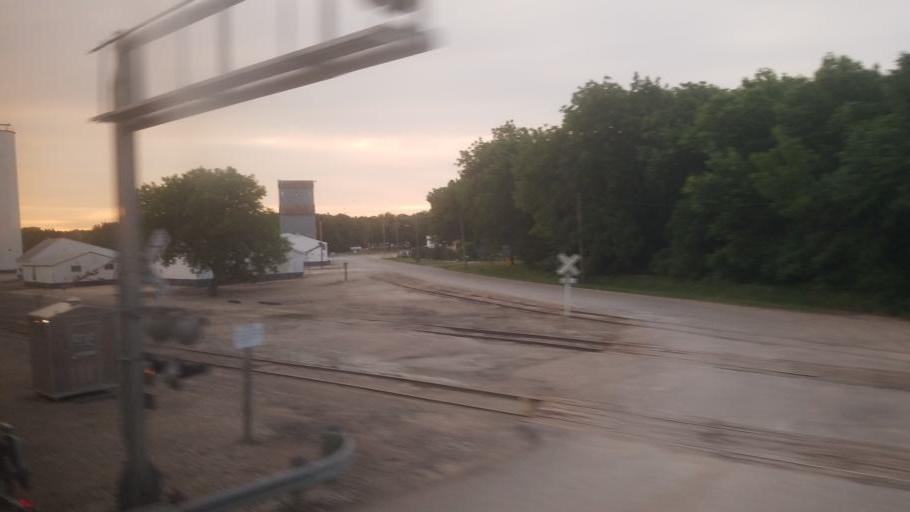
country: US
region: Kansas
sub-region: Marion County
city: Peabody
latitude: 38.1640
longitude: -97.1069
